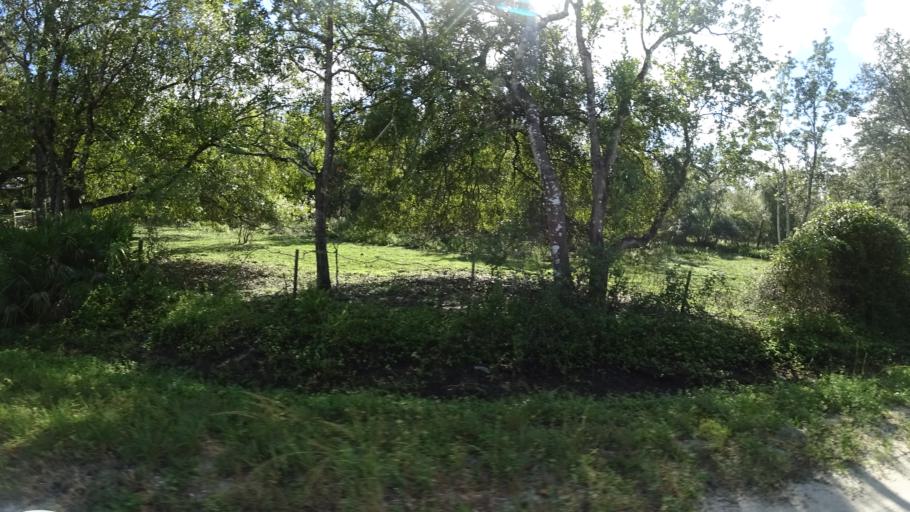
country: US
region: Florida
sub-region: Sarasota County
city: Lake Sarasota
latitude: 27.3169
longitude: -82.2198
